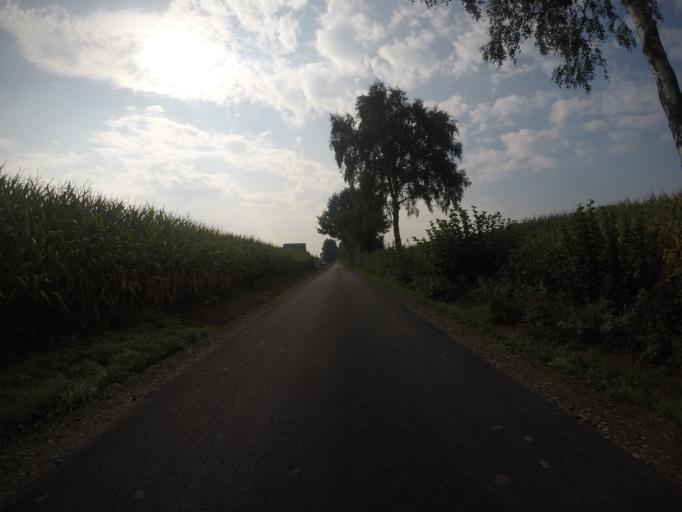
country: DE
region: North Rhine-Westphalia
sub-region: Regierungsbezirk Dusseldorf
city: Bocholt
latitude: 51.8249
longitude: 6.5547
